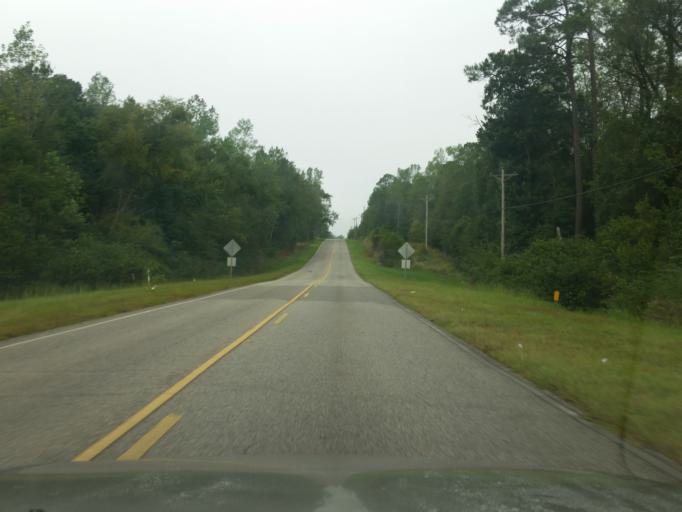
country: US
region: Alabama
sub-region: Baldwin County
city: Bay Minette
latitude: 30.8527
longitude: -87.8080
